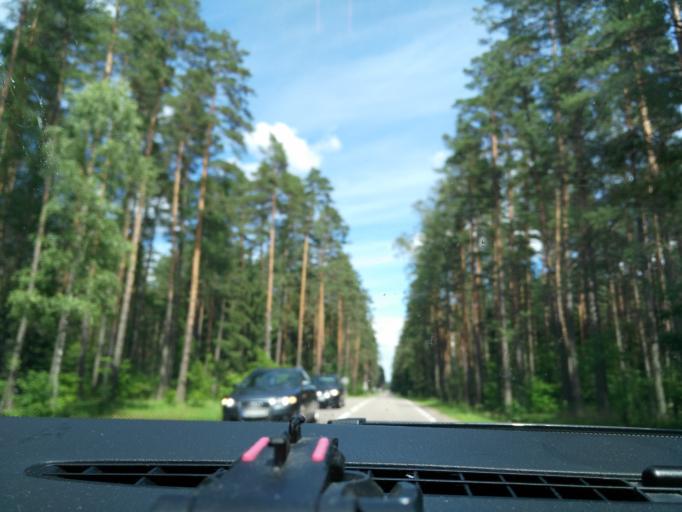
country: PL
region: Podlasie
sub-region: Powiat sejnenski
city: Krasnopol
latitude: 53.9650
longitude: 23.2395
